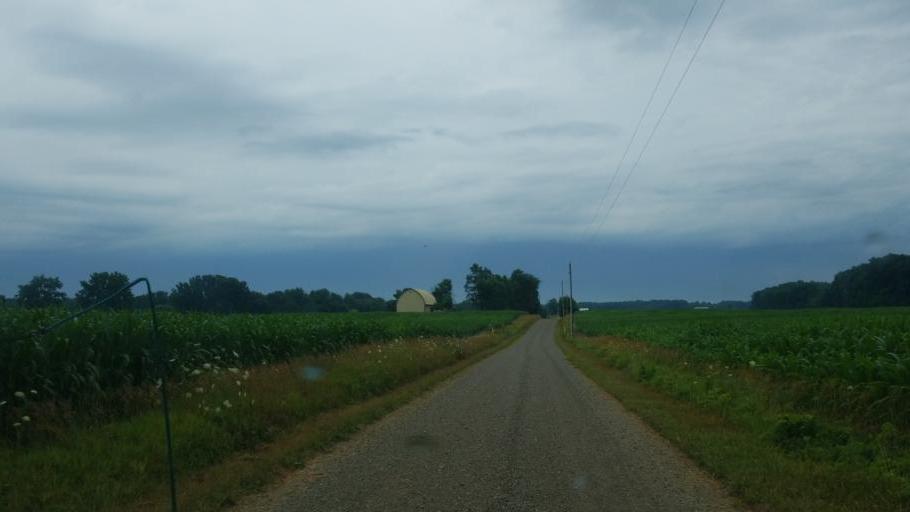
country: US
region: Indiana
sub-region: Steuben County
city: Hamilton
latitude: 41.5053
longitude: -84.9189
